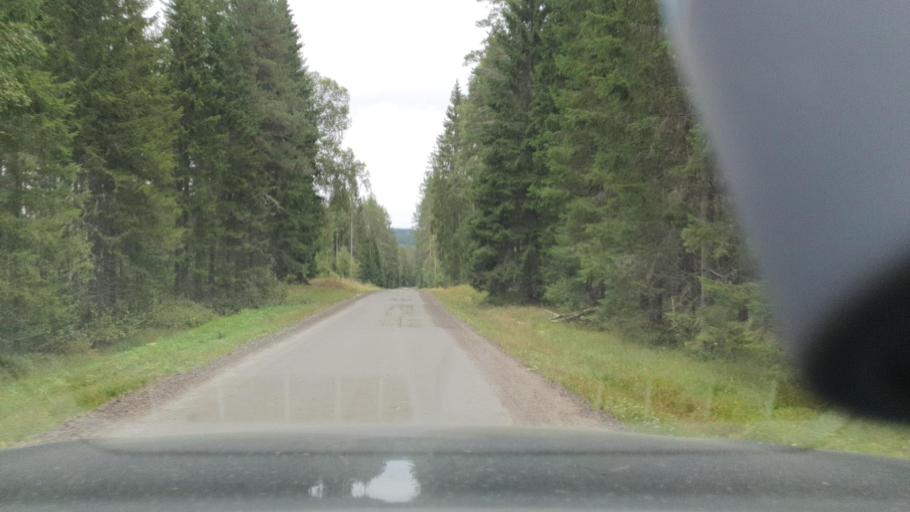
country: SE
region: Vaermland
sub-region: Torsby Kommun
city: Torsby
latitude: 60.3835
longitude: 12.8863
